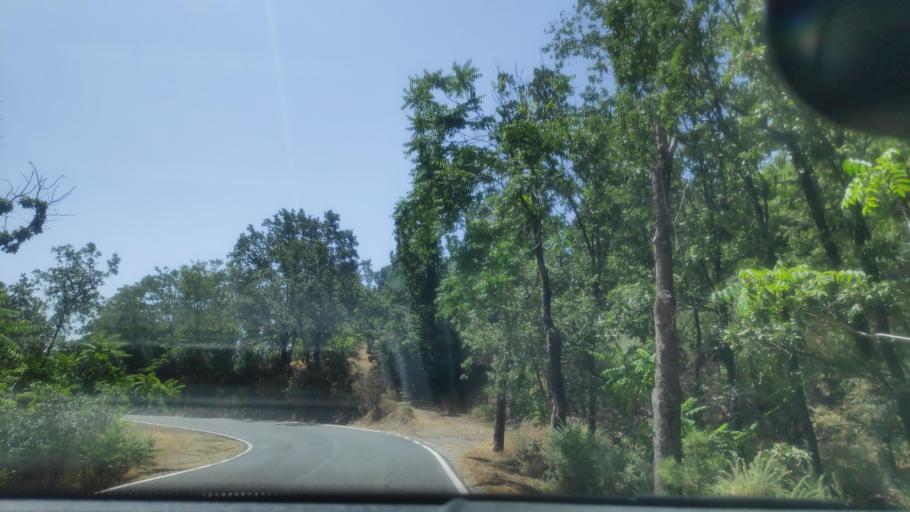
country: ES
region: Andalusia
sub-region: Provincia de Granada
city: Busquistar
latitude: 36.9692
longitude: -3.2810
